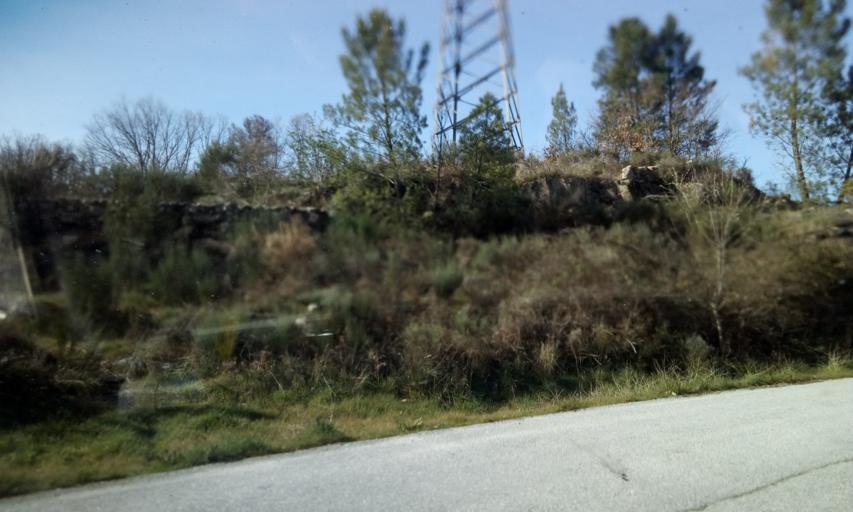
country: PT
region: Guarda
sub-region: Celorico da Beira
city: Celorico da Beira
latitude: 40.6457
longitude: -7.3955
